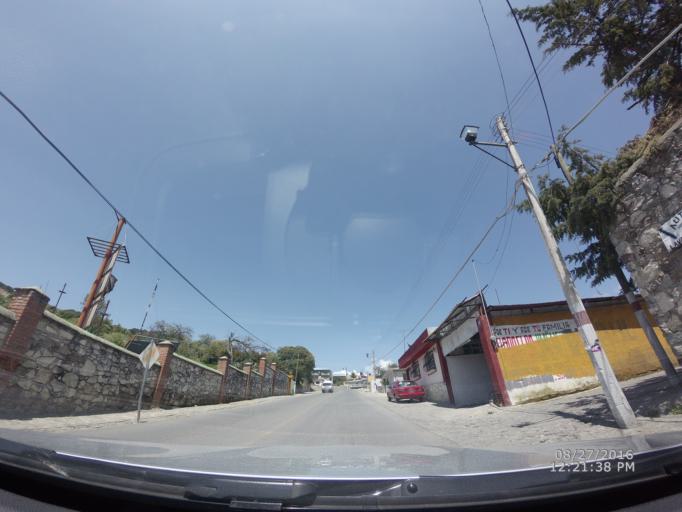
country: MX
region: Hidalgo
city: Mineral del Monte
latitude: 20.1363
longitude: -98.6782
